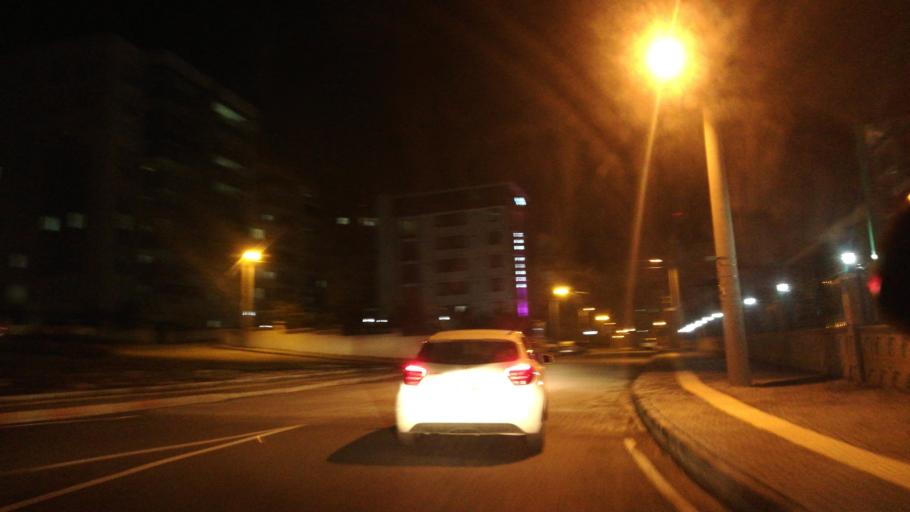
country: TR
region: Kahramanmaras
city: Kahramanmaras
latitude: 37.5974
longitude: 36.8842
